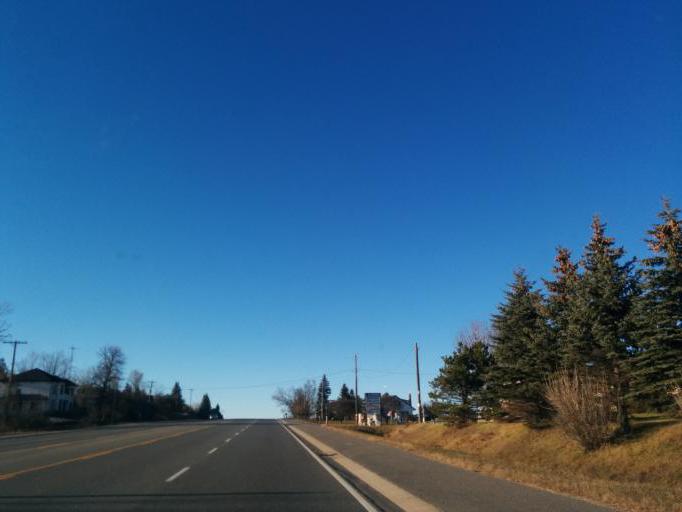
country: CA
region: Ontario
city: Orangeville
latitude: 43.8137
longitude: -79.9328
